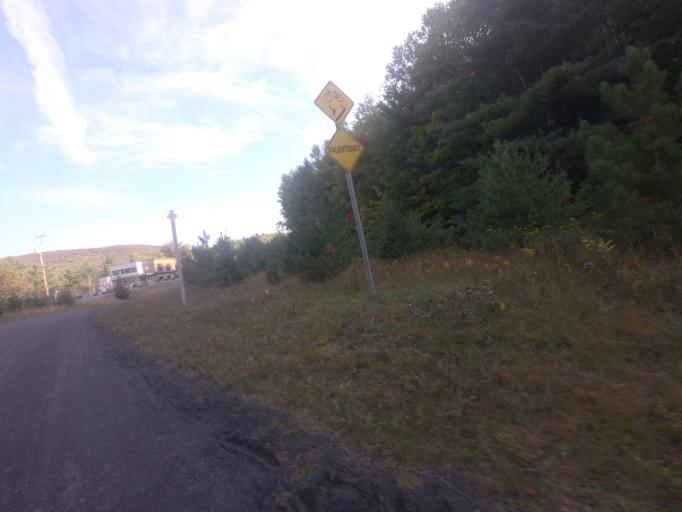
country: CA
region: Quebec
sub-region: Laurentides
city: Sainte-Adele
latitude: 45.9886
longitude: -74.1185
